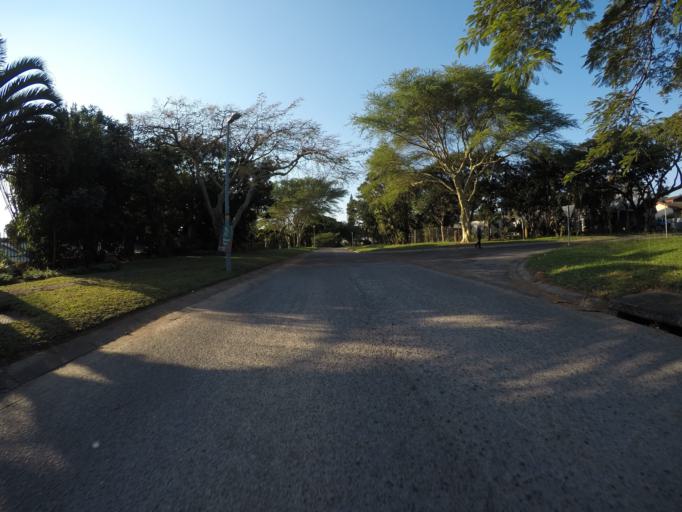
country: ZA
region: KwaZulu-Natal
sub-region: uThungulu District Municipality
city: Richards Bay
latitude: -28.7746
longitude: 32.1065
